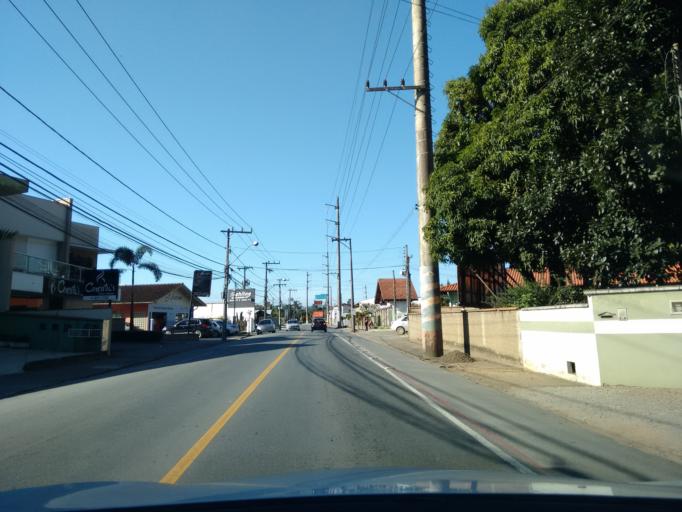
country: BR
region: Santa Catarina
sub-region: Jaragua Do Sul
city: Jaragua do Sul
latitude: -26.4954
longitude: -49.0719
